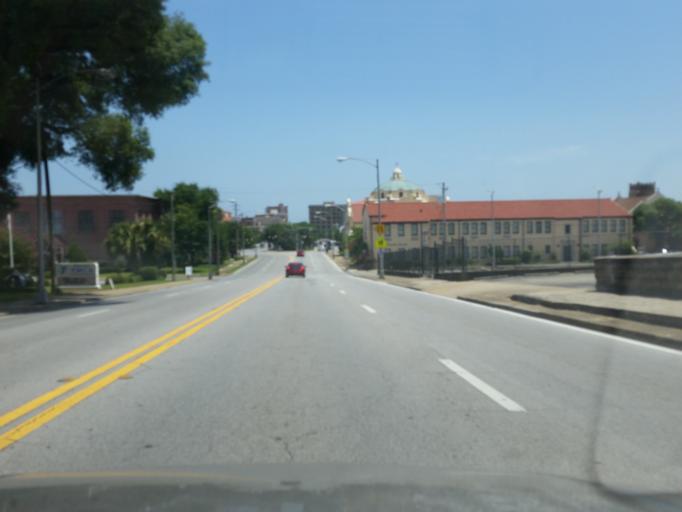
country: US
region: Florida
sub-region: Escambia County
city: Pensacola
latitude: 30.4183
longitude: -87.2167
